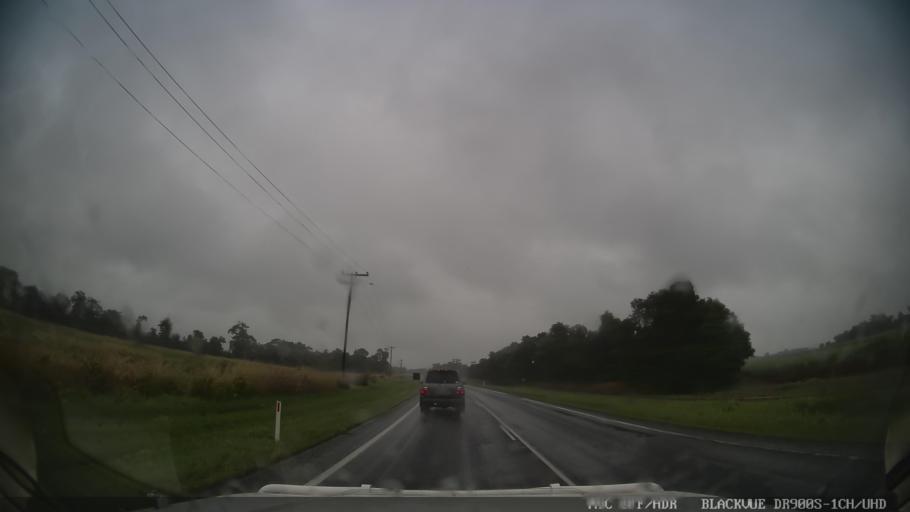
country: AU
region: Queensland
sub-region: Cassowary Coast
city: Innisfail
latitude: -17.6571
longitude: 146.0365
